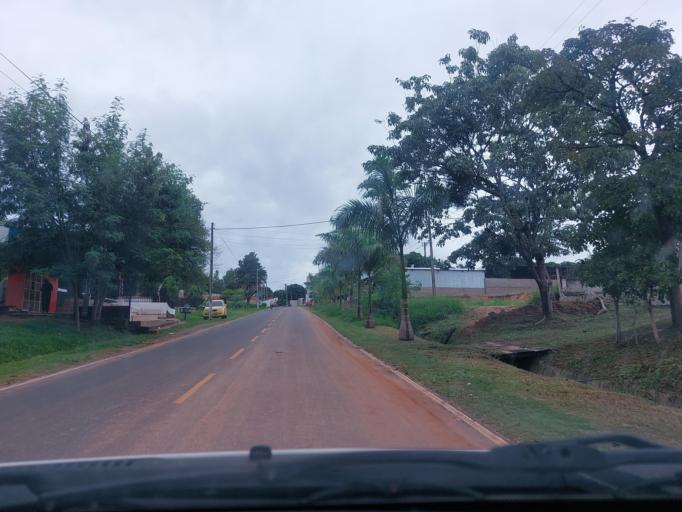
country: PY
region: San Pedro
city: Guayaybi
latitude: -24.6570
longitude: -56.4384
